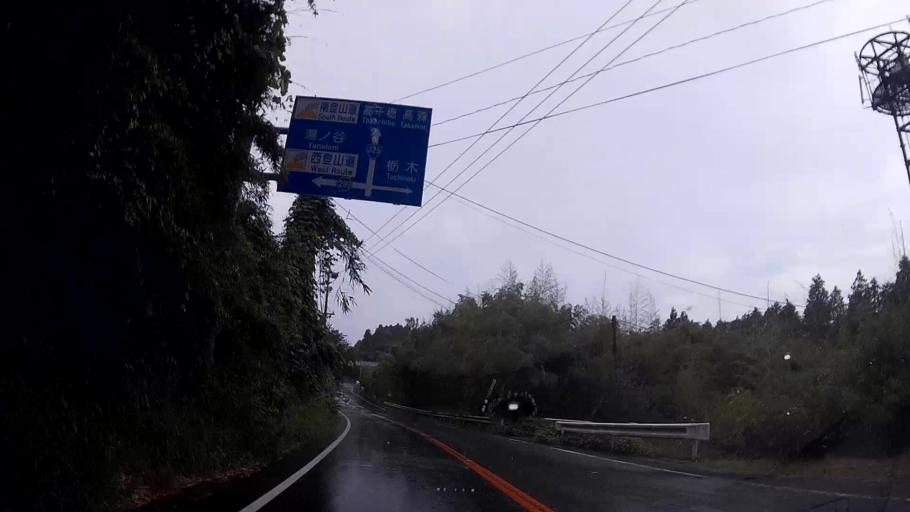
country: JP
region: Kumamoto
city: Aso
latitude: 32.8717
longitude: 130.9939
